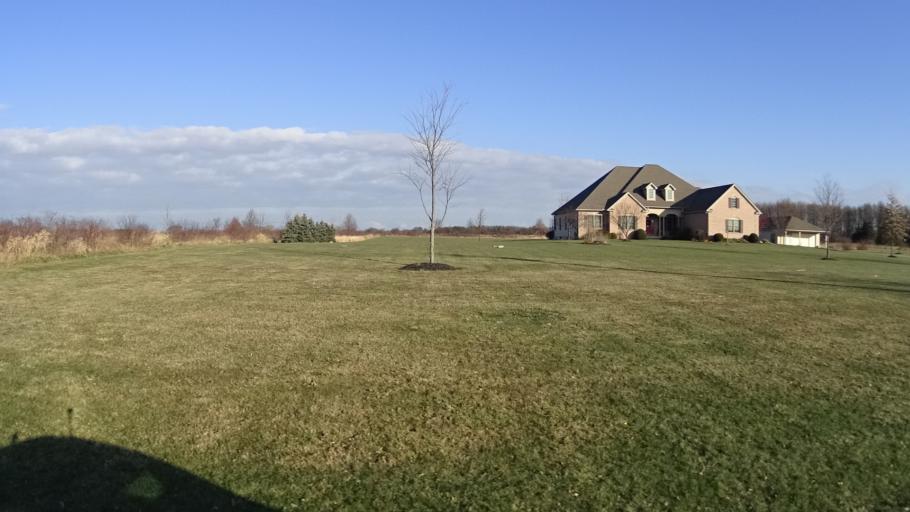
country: US
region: Ohio
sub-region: Lorain County
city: Oberlin
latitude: 41.2504
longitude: -82.2513
